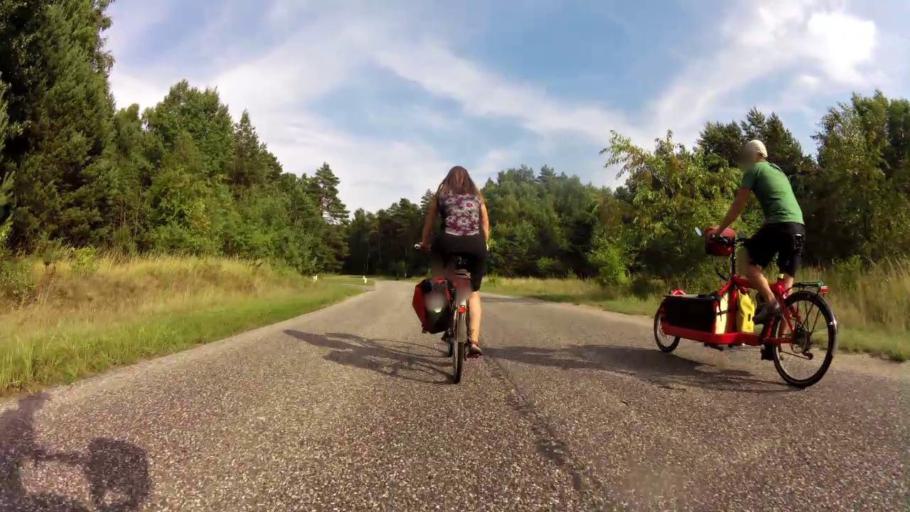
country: PL
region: West Pomeranian Voivodeship
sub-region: Powiat drawski
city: Drawsko Pomorskie
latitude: 53.4702
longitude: 15.7294
